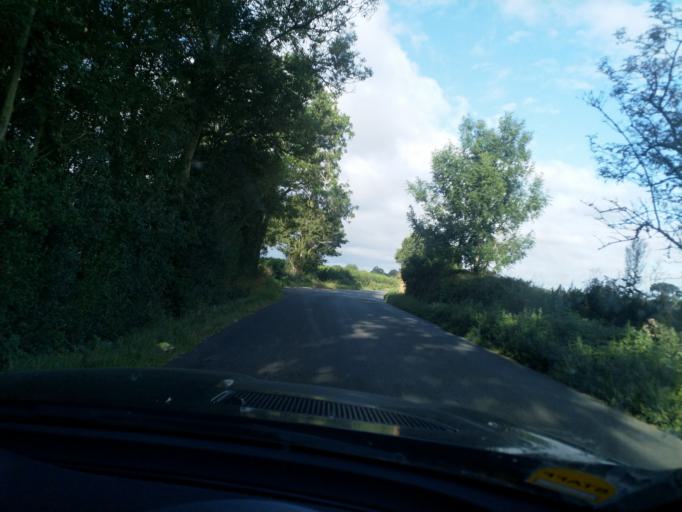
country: GB
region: England
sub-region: Suffolk
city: Elmswell
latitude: 52.2338
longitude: 0.9607
